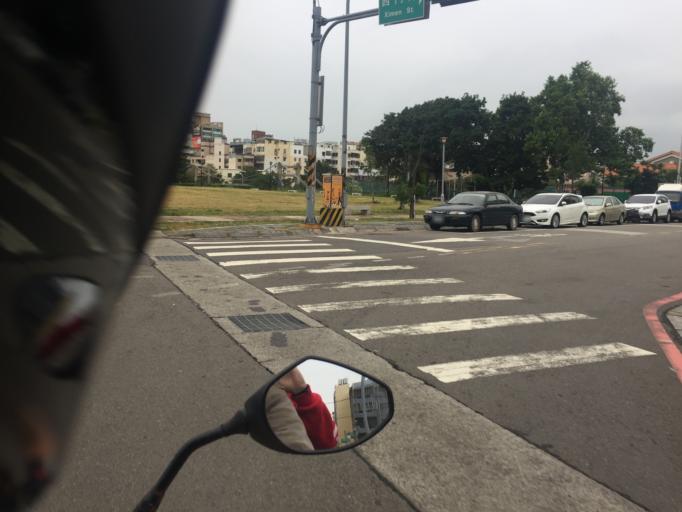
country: TW
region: Taiwan
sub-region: Hsinchu
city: Hsinchu
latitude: 24.7988
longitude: 120.9593
